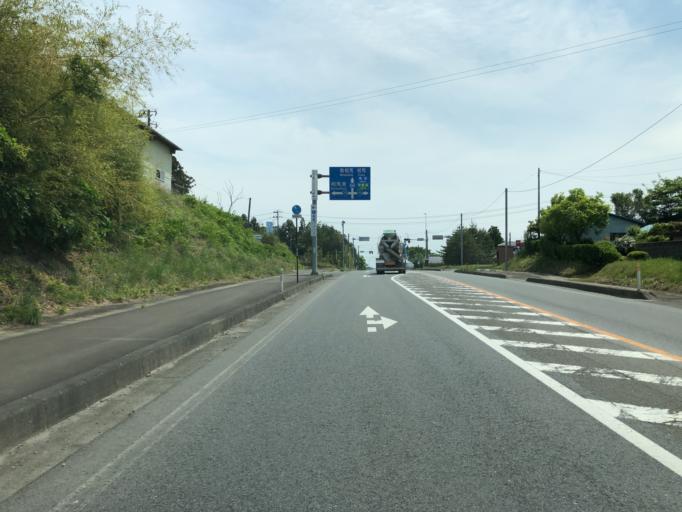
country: JP
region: Miyagi
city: Marumori
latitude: 37.8383
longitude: 140.9182
